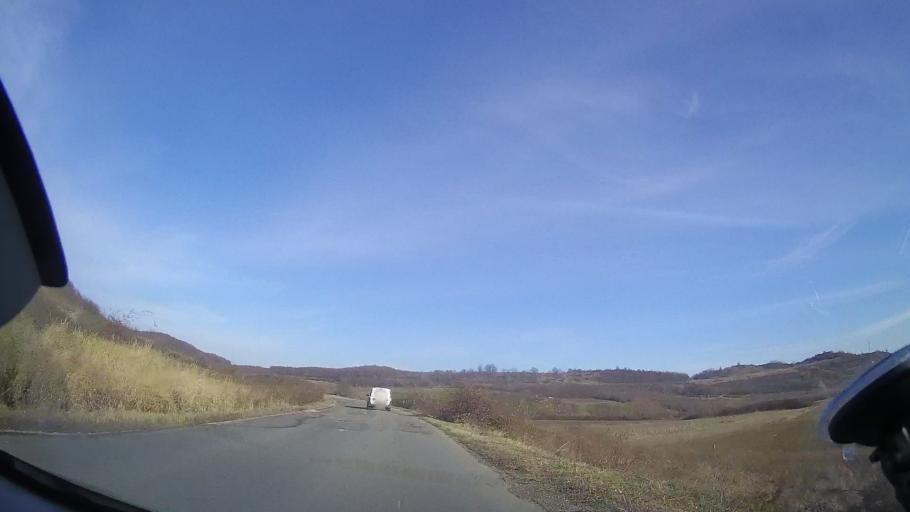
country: RO
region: Bihor
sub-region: Comuna Tileagd
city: Tileagd
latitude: 47.0851
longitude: 22.2329
